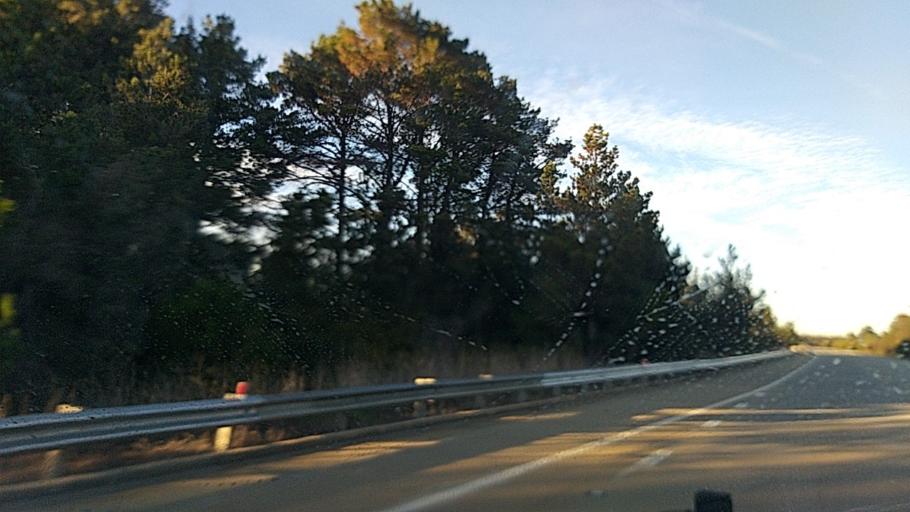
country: AU
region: New South Wales
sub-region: Yass Valley
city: Gundaroo
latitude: -35.1451
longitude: 149.3333
